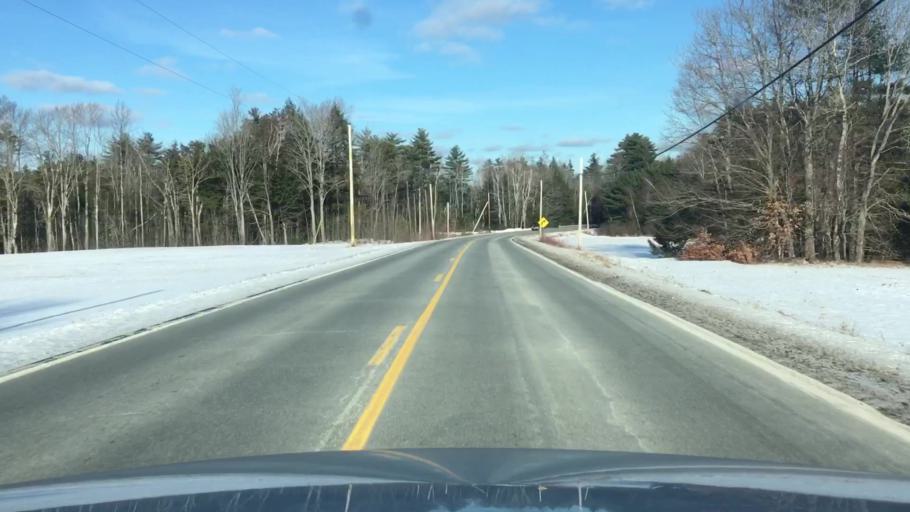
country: US
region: Maine
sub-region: Penobscot County
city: Holden
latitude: 44.7498
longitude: -68.6119
